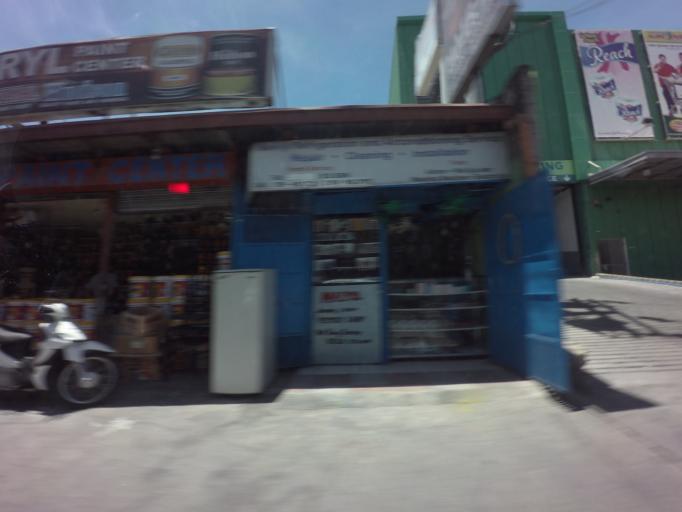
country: PH
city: Sambayanihan People's Village
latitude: 14.4972
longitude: 121.0134
